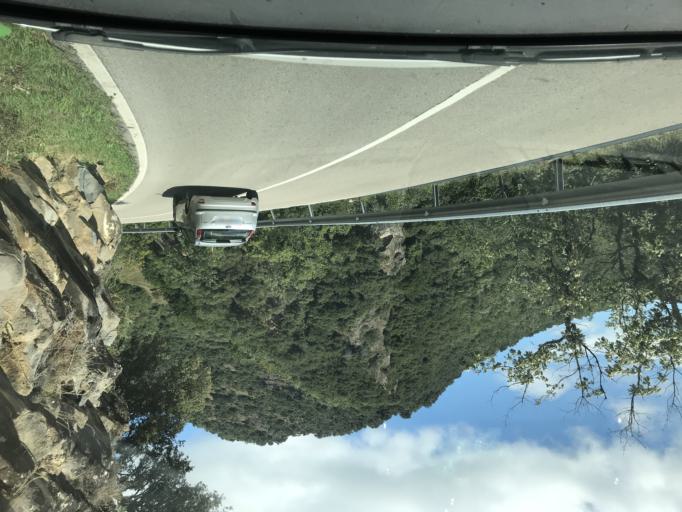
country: ES
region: Cantabria
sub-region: Provincia de Cantabria
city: Cabezon de Liebana
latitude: 43.0759
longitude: -4.5052
